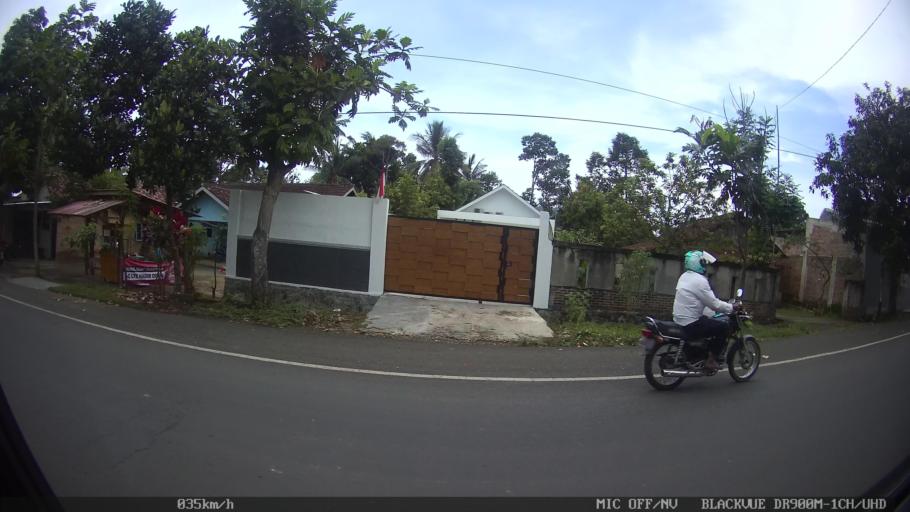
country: ID
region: Lampung
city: Bandarlampung
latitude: -5.4353
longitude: 105.2266
